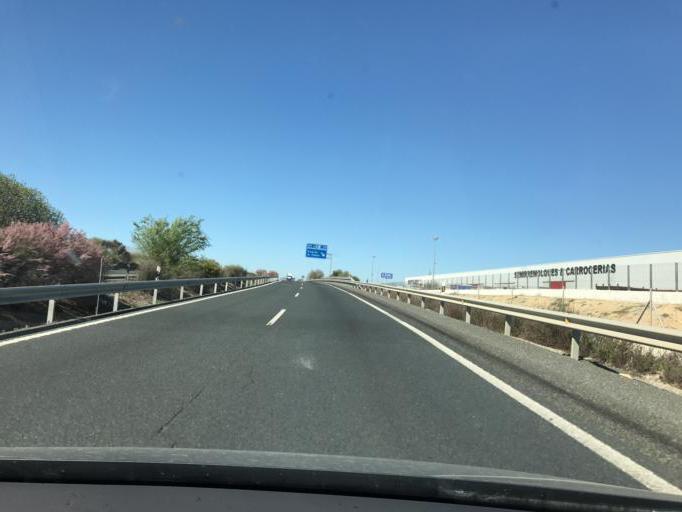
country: ES
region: Andalusia
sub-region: Provincia de Malaga
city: Villanueva de Tapia
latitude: 37.1428
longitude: -4.2664
